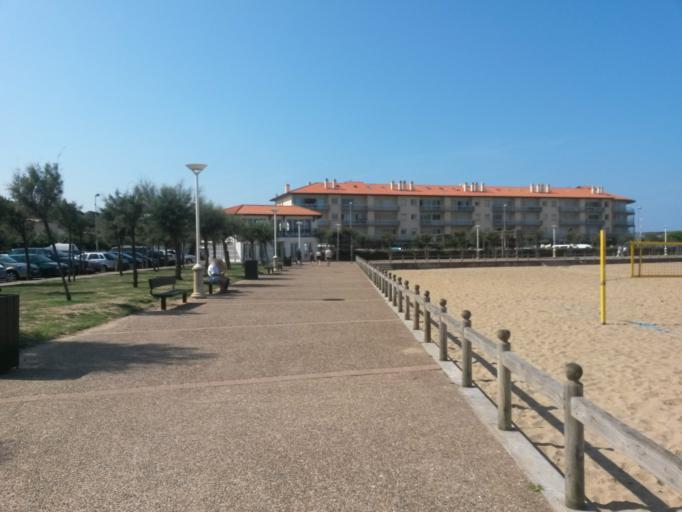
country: FR
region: Aquitaine
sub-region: Departement des Pyrenees-Atlantiques
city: Biarritz
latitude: 43.5015
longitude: -1.5401
